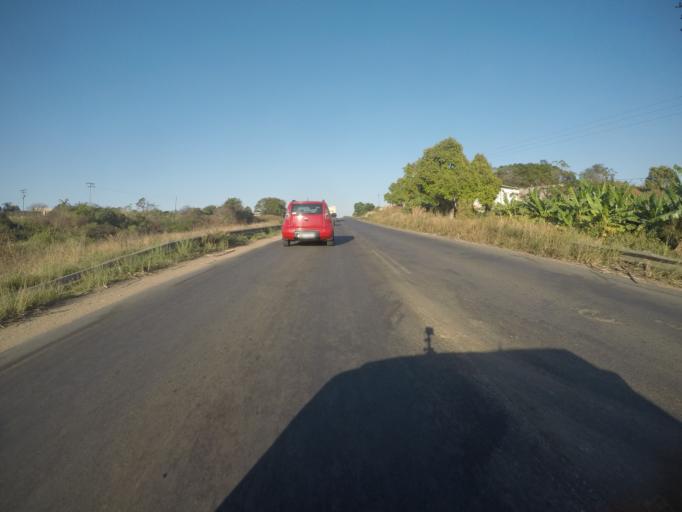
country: ZA
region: KwaZulu-Natal
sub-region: iLembe District Municipality
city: Stanger
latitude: -29.4025
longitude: 31.2512
